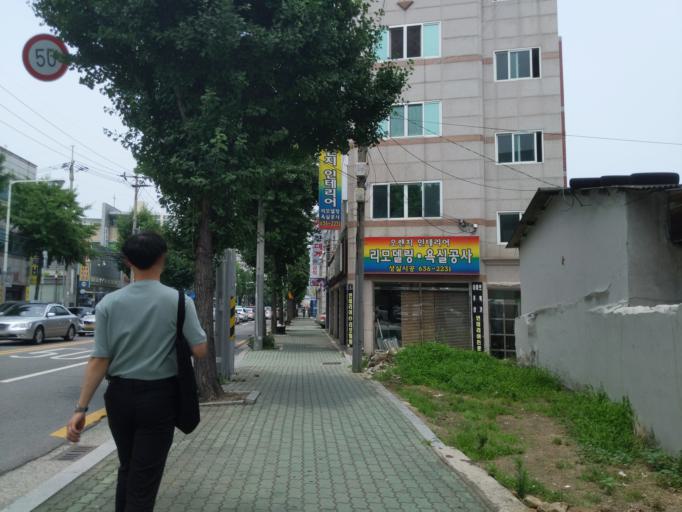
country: KR
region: Daegu
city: Hwawon
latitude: 35.8093
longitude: 128.5269
